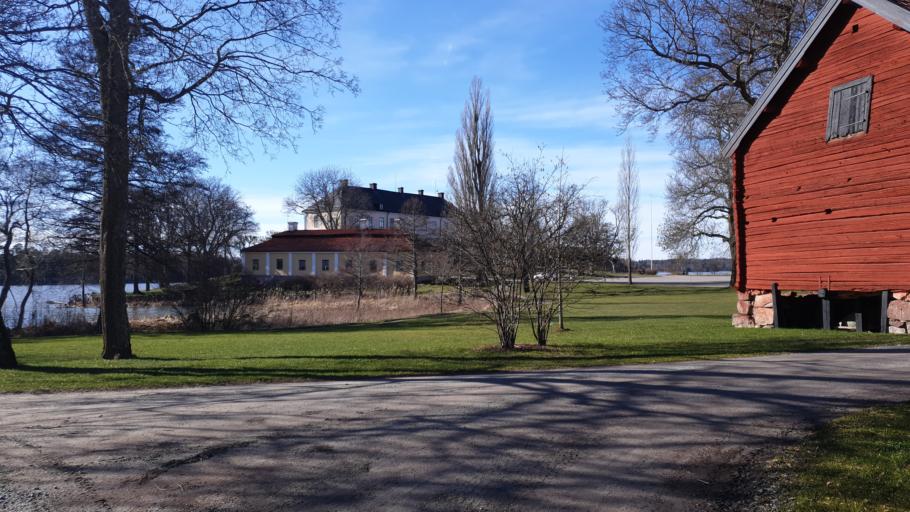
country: SE
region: Soedermanland
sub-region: Strangnas Kommun
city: Stallarholmen
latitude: 59.4721
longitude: 17.2489
